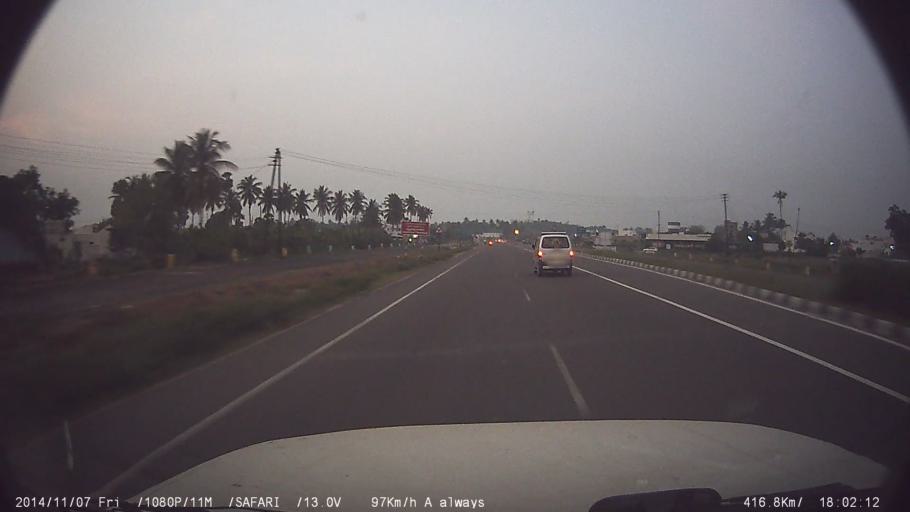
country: IN
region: Tamil Nadu
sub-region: Erode
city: Bhavani
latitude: 11.3891
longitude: 77.6530
